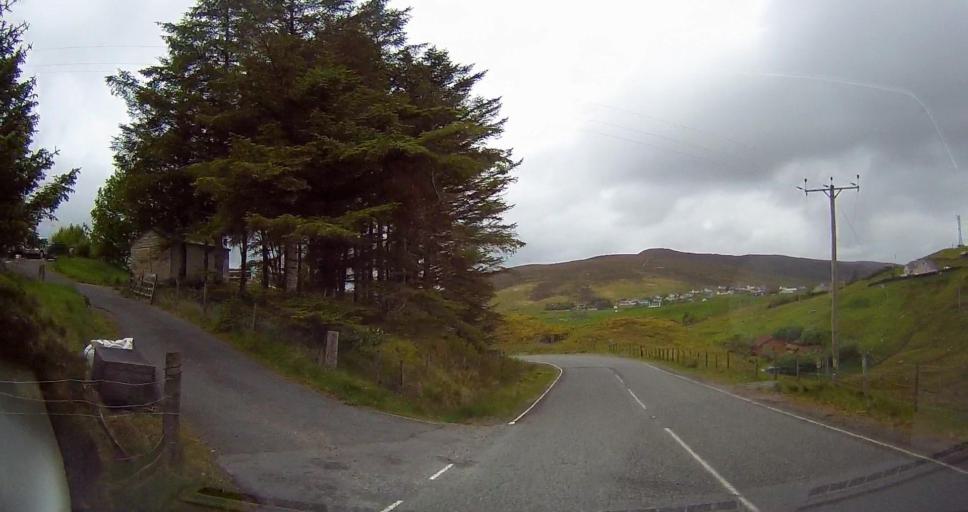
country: GB
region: Scotland
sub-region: Shetland Islands
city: Lerwick
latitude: 60.3499
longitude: -1.2596
